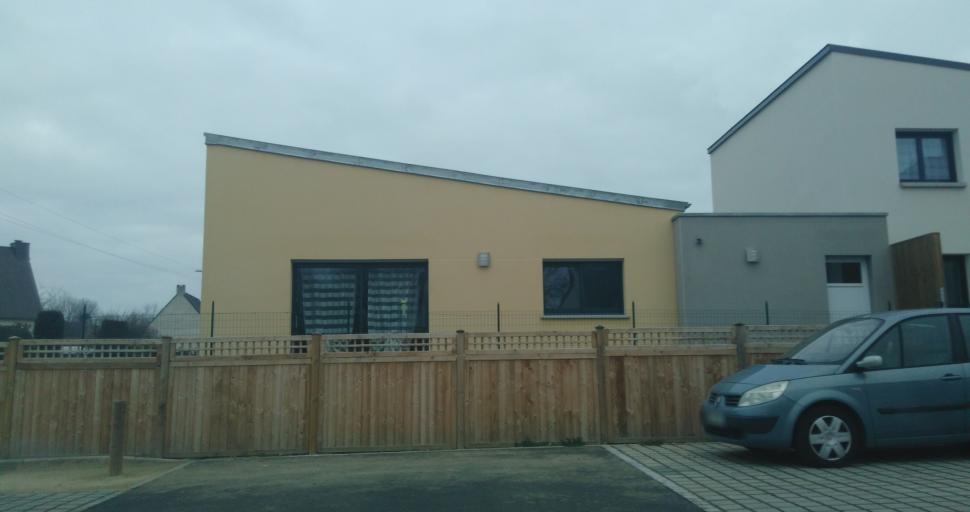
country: FR
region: Brittany
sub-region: Departement d'Ille-et-Vilaine
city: Romille
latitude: 48.2208
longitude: -1.8917
